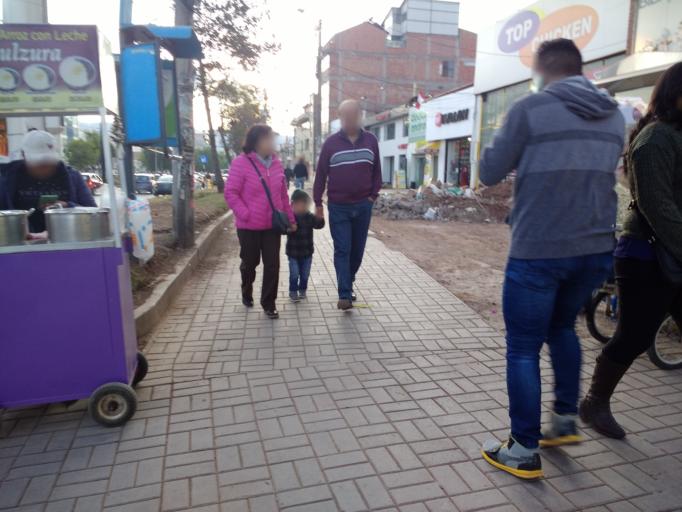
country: PE
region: Cusco
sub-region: Provincia de Cusco
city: Cusco
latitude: -13.5256
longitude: -71.9517
